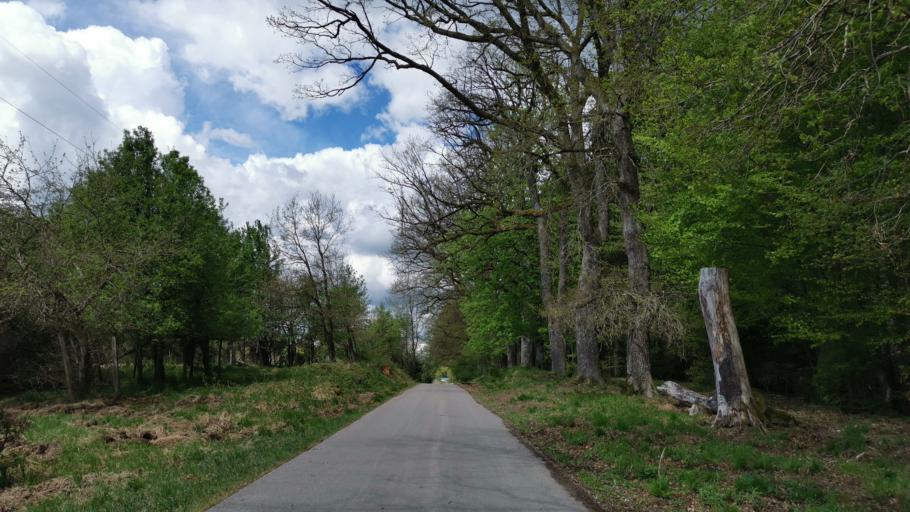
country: DE
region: Bavaria
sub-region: Upper Bavaria
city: Baierbrunn
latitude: 48.0512
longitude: 11.4645
